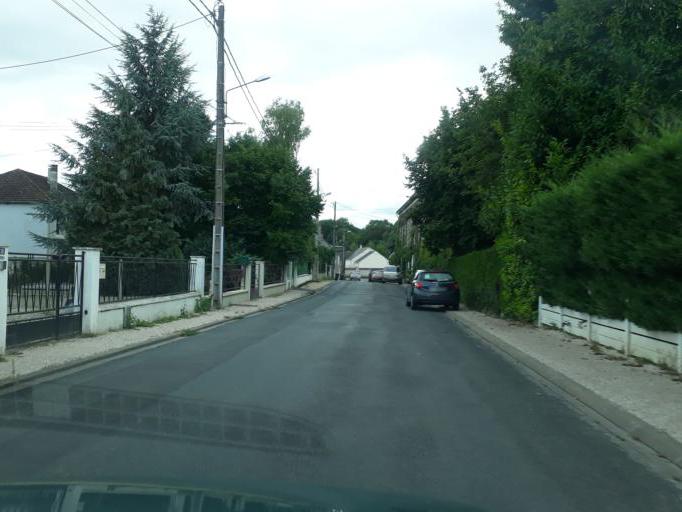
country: FR
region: Centre
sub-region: Departement du Loiret
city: Meung-sur-Loire
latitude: 47.8329
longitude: 1.7030
